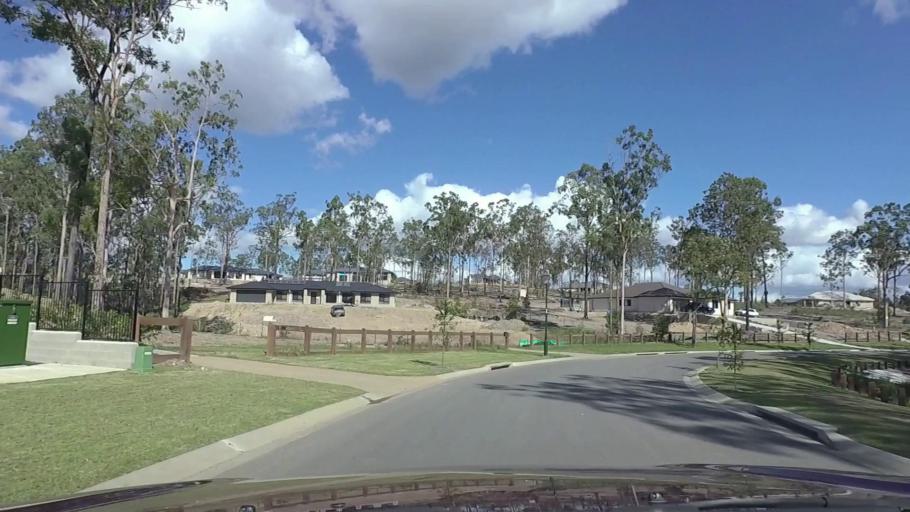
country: AU
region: Queensland
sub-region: Ipswich
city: Springfield Lakes
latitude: -27.7500
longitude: 152.9212
